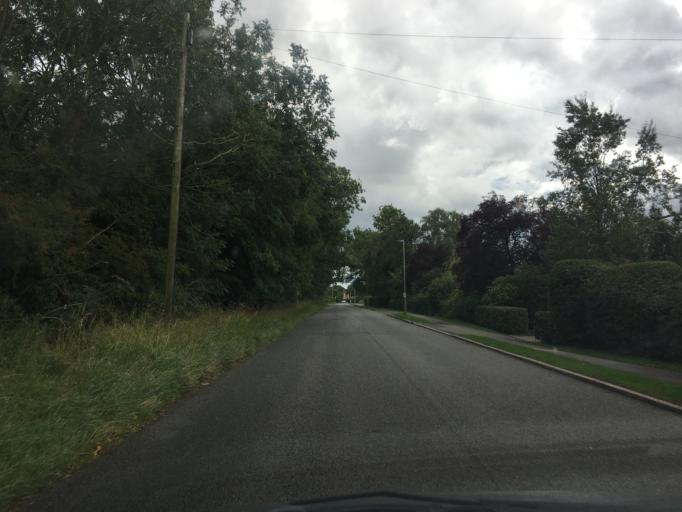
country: GB
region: England
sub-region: Leicestershire
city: Lutterworth
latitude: 52.4722
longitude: -1.2105
